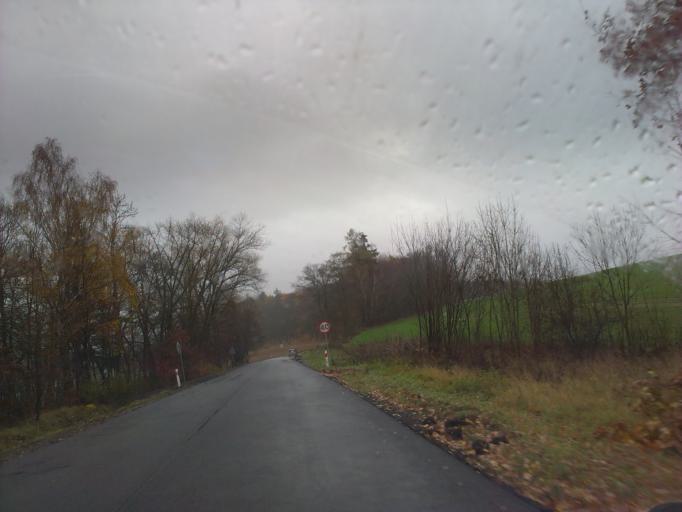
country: PL
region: West Pomeranian Voivodeship
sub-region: Powiat szczecinecki
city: Borne Sulinowo
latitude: 53.6181
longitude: 16.5407
